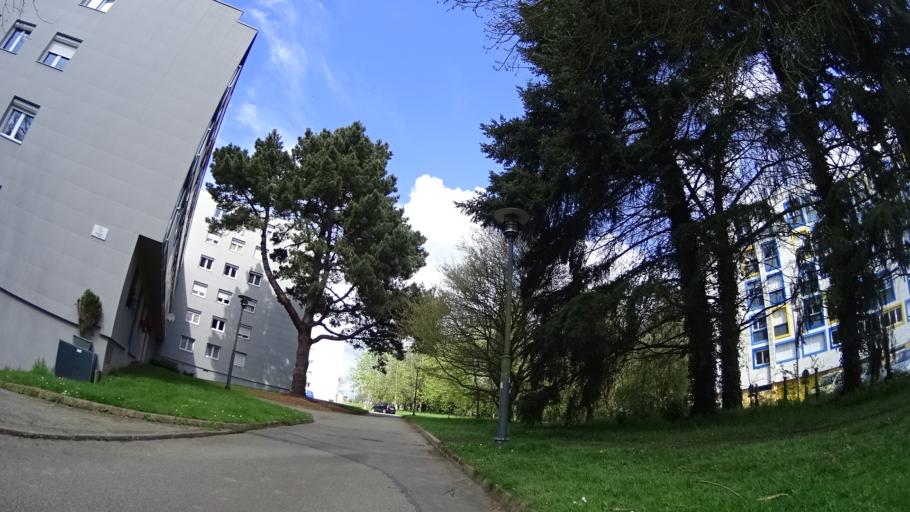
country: FR
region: Brittany
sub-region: Departement d'Ille-et-Vilaine
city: Rennes
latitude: 48.1315
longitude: -1.6649
